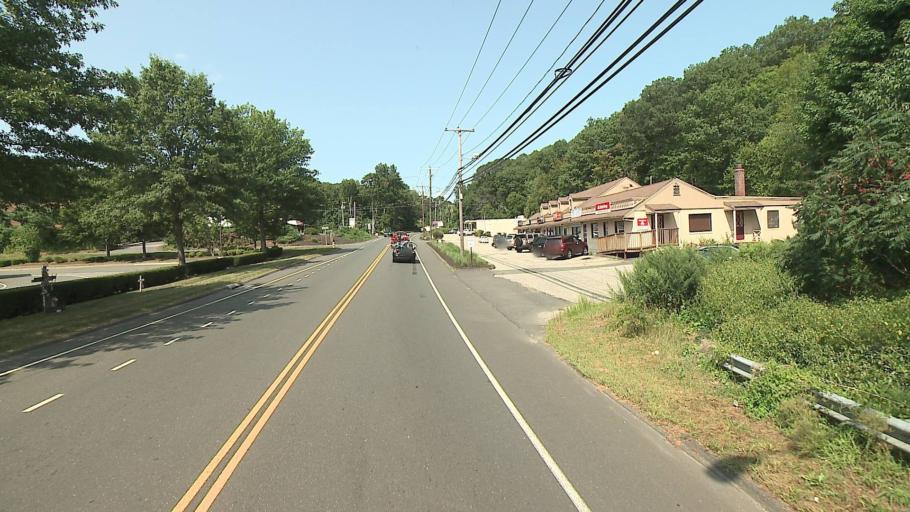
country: US
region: Connecticut
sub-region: Fairfield County
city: Newtown
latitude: 41.3254
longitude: -73.2671
